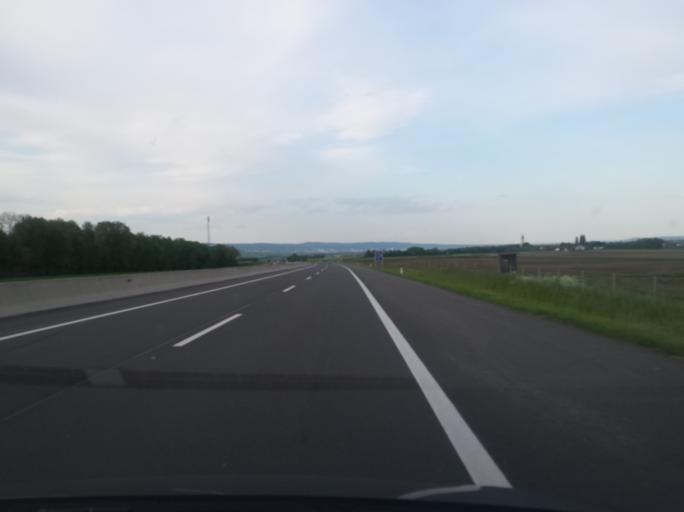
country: AT
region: Burgenland
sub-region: Politischer Bezirk Mattersburg
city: Pottelsdorf
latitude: 47.7664
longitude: 16.4240
